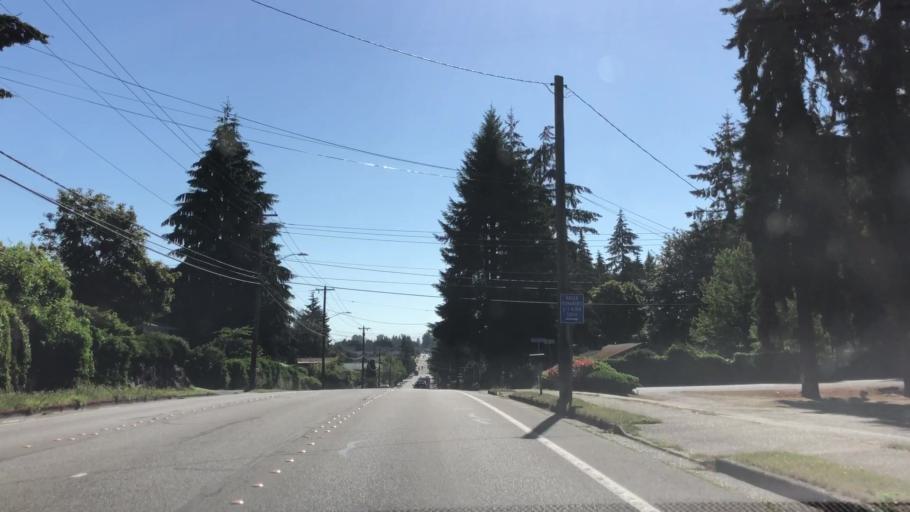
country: US
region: Washington
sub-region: Snohomish County
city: Lynnwood
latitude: 47.8175
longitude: -122.3067
